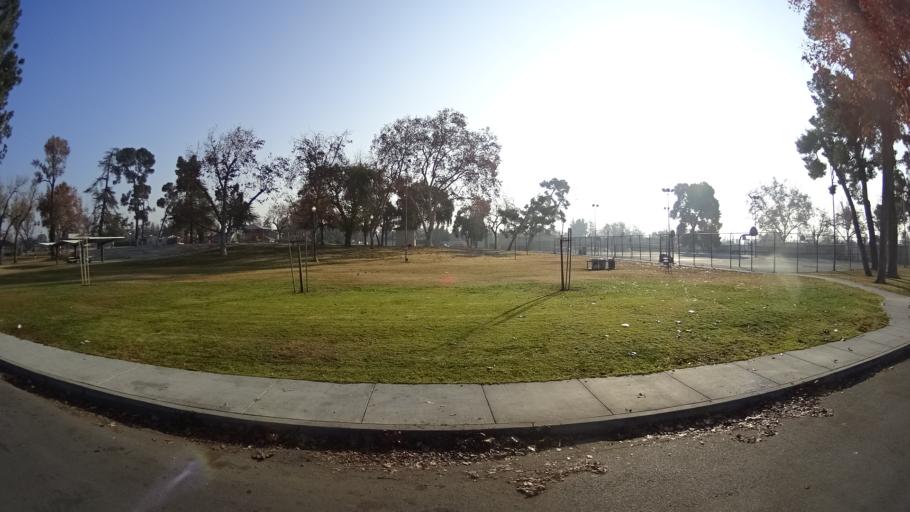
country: US
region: California
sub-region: Kern County
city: Bakersfield
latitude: 35.3886
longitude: -118.9870
